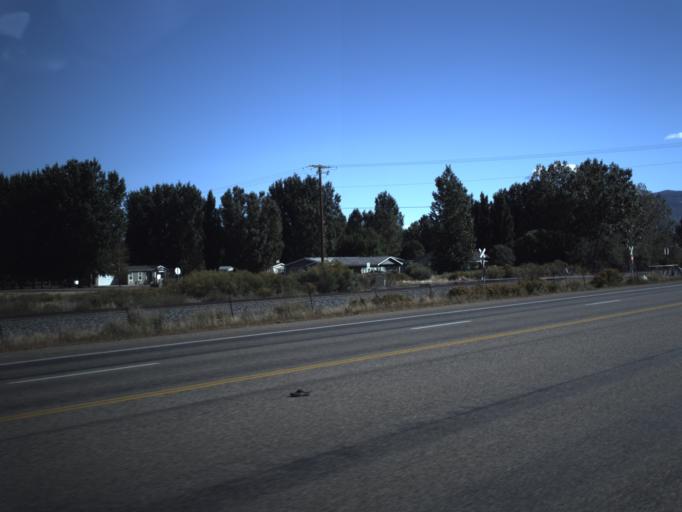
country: US
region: Utah
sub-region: Iron County
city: Cedar City
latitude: 37.6849
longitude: -113.1373
